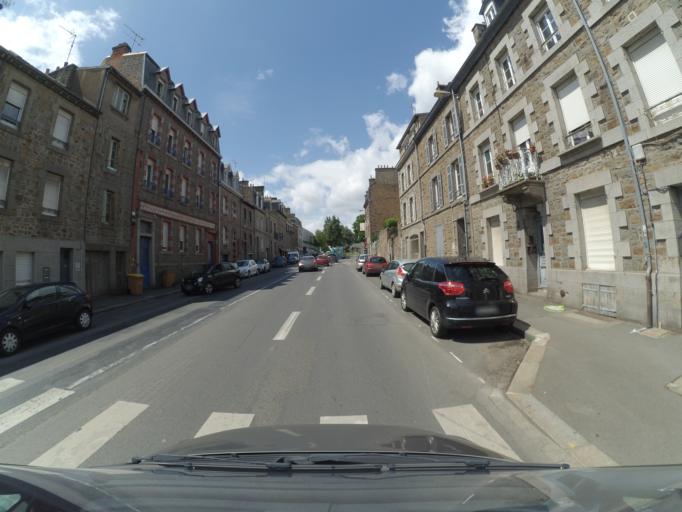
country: FR
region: Brittany
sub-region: Departement des Cotes-d'Armor
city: Saint-Brieuc
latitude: 48.5086
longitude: -2.7703
